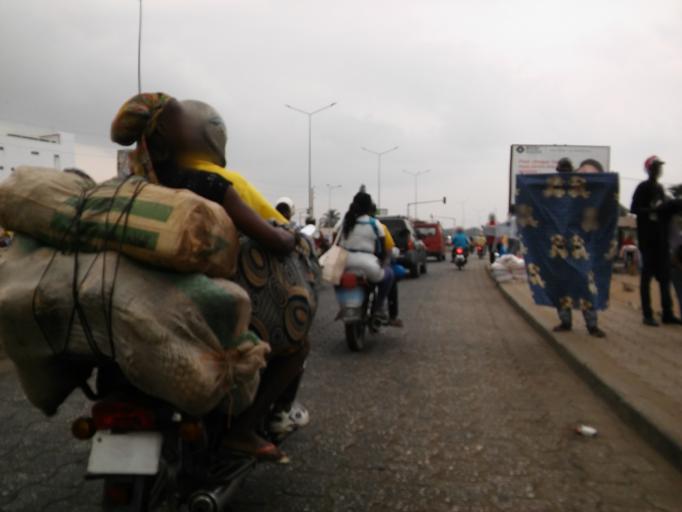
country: BJ
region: Littoral
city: Cotonou
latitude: 6.3851
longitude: 2.3749
